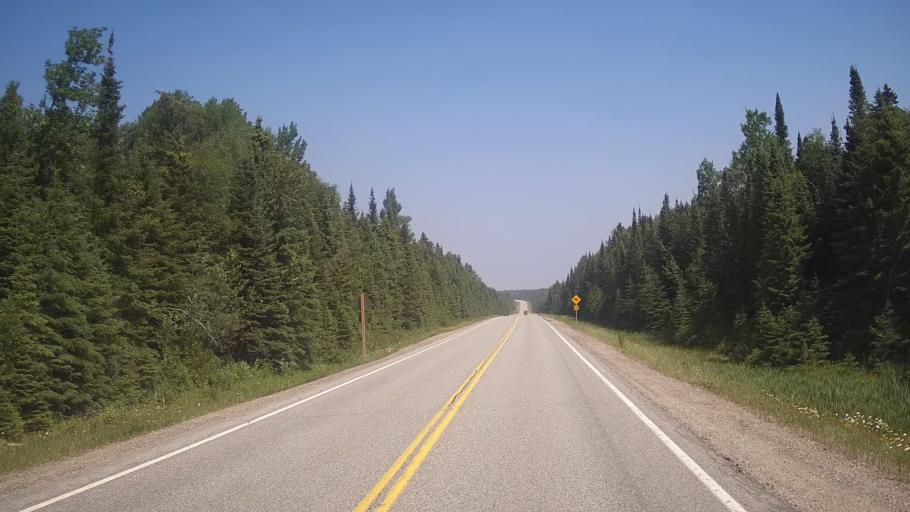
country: CA
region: Ontario
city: Timmins
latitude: 48.0876
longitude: -81.5954
